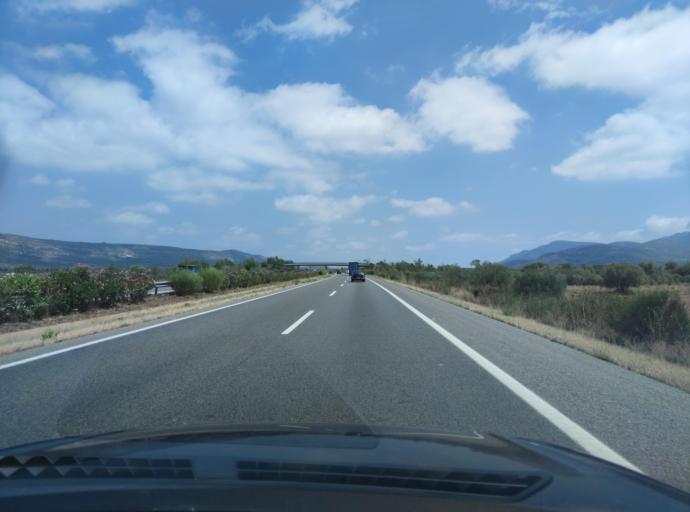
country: ES
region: Catalonia
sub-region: Provincia de Tarragona
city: Ulldecona
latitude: 40.5970
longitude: 0.4702
